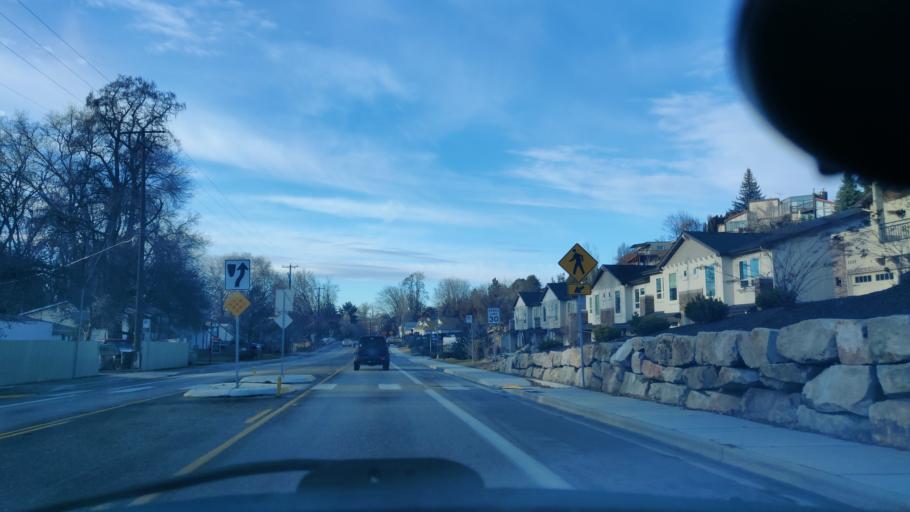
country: US
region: Idaho
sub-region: Ada County
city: Garden City
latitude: 43.6447
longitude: -116.2164
